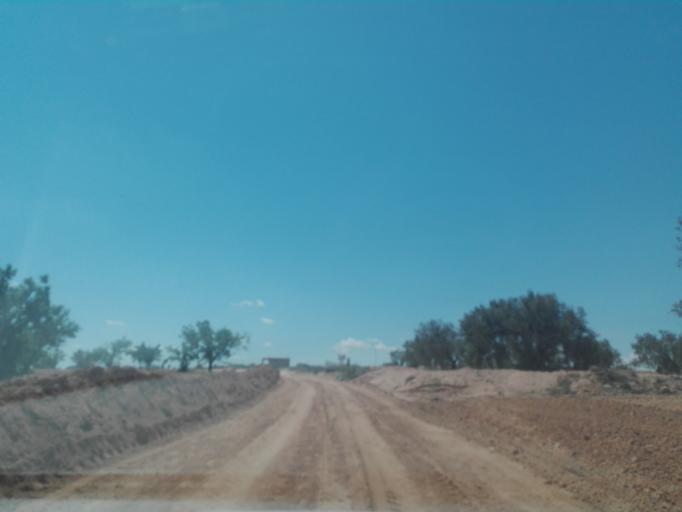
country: TN
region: Safaqis
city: Bi'r `Ali Bin Khalifah
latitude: 34.7896
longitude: 10.3372
